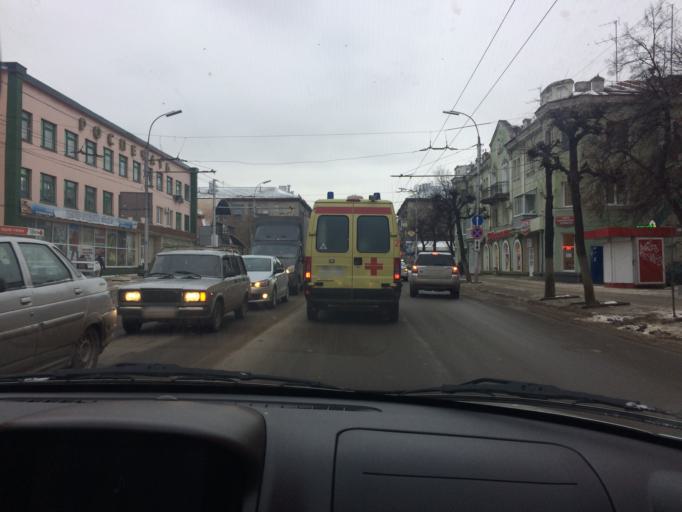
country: RU
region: Rjazan
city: Ryazan'
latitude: 54.6286
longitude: 39.7163
